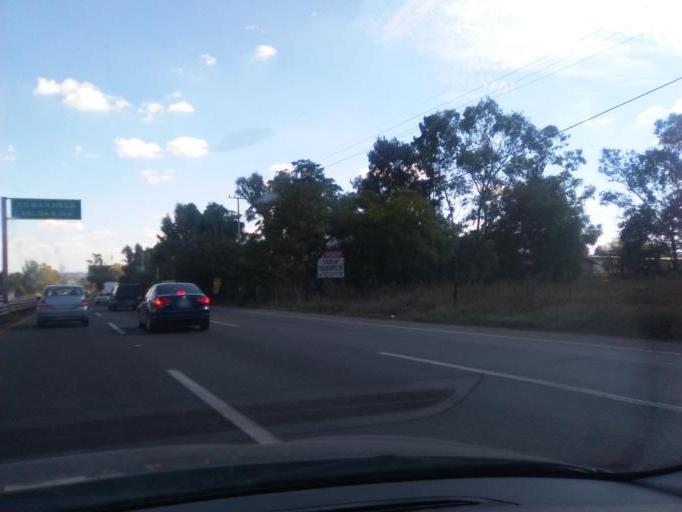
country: MX
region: Guanajuato
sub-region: Silao de la Victoria
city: El Refugio de los Sauces
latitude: 21.0361
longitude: -101.5535
